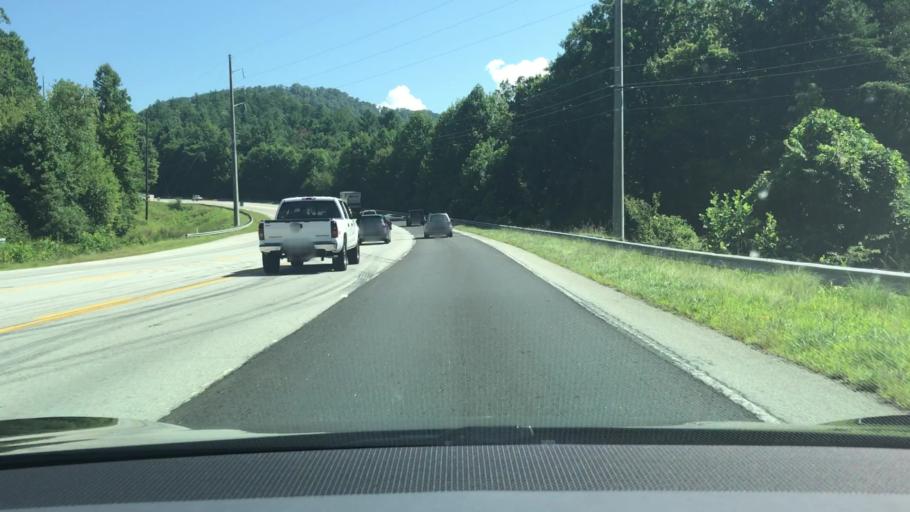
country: US
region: Georgia
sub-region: Rabun County
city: Clayton
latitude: 34.8889
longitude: -83.3927
